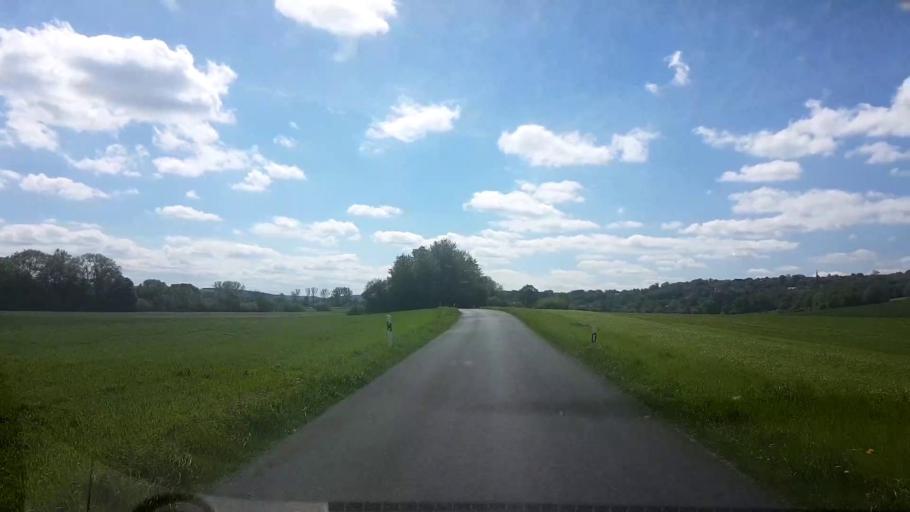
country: DE
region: Bavaria
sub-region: Upper Franconia
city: Grossheirath
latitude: 50.1569
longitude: 10.9186
